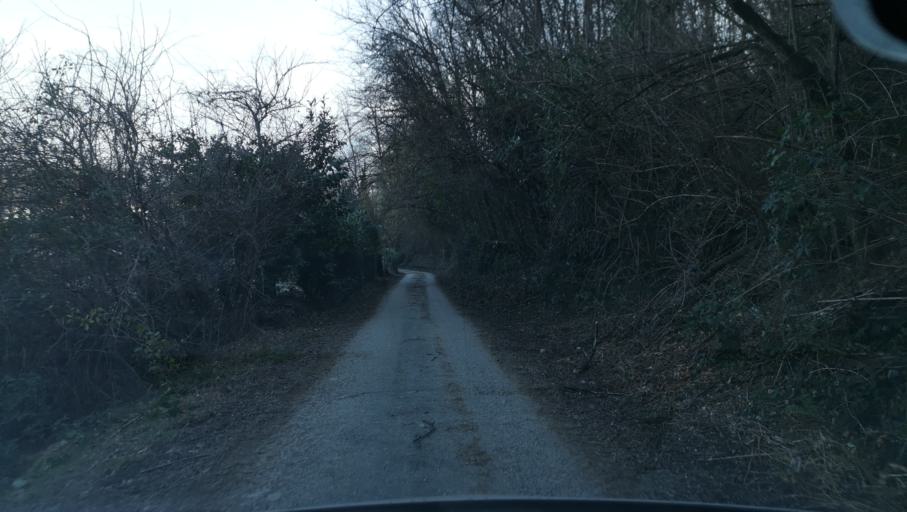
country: IT
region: Piedmont
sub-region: Provincia di Torino
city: Gassino Torinese
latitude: 45.1100
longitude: 7.8270
